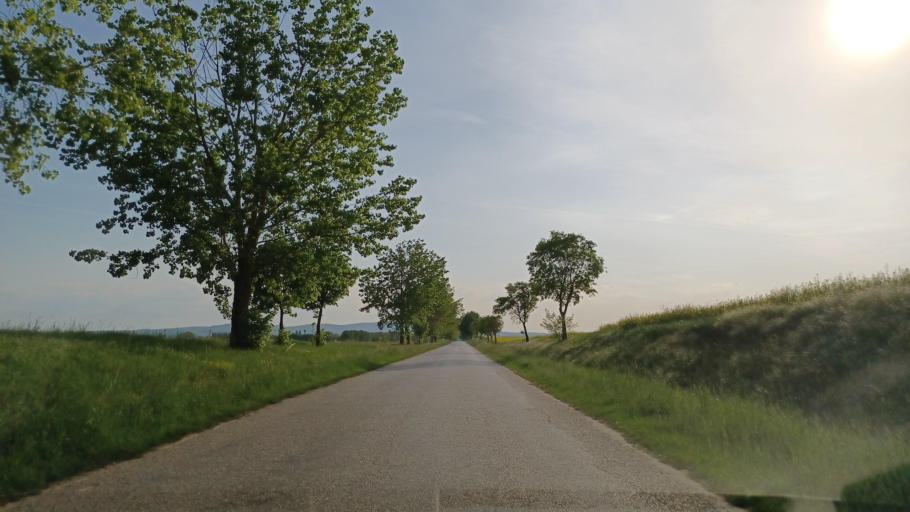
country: HU
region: Baranya
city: Kozarmisleny
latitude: 45.9514
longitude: 18.3749
